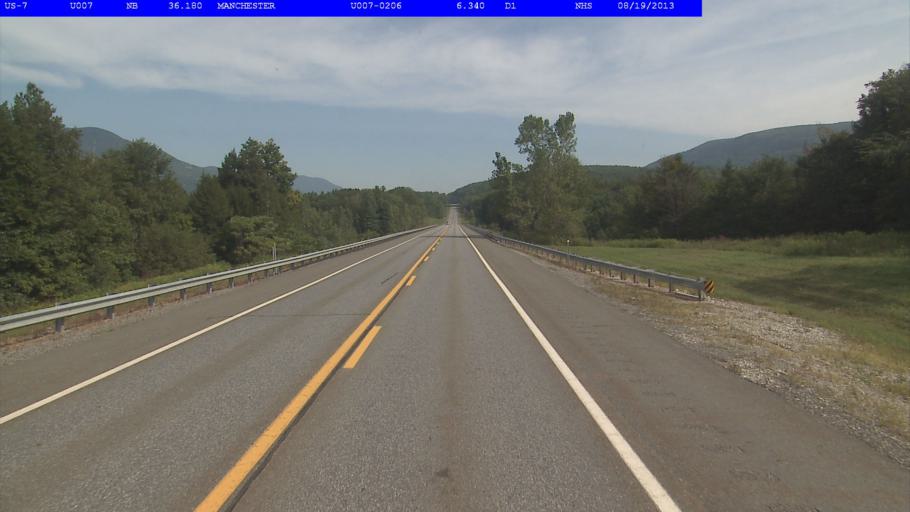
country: US
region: Vermont
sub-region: Bennington County
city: Manchester Center
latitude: 43.1938
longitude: -73.0135
